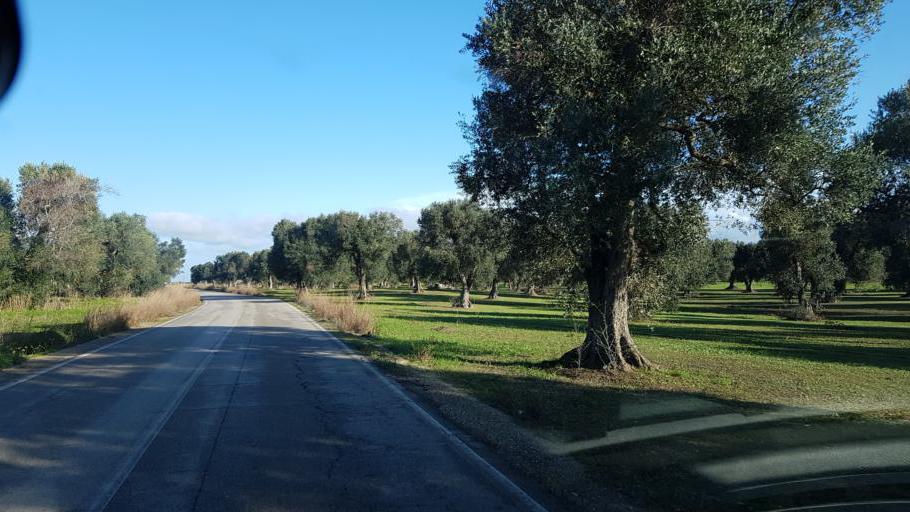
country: IT
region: Apulia
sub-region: Provincia di Brindisi
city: Tuturano
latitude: 40.5637
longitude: 17.9489
